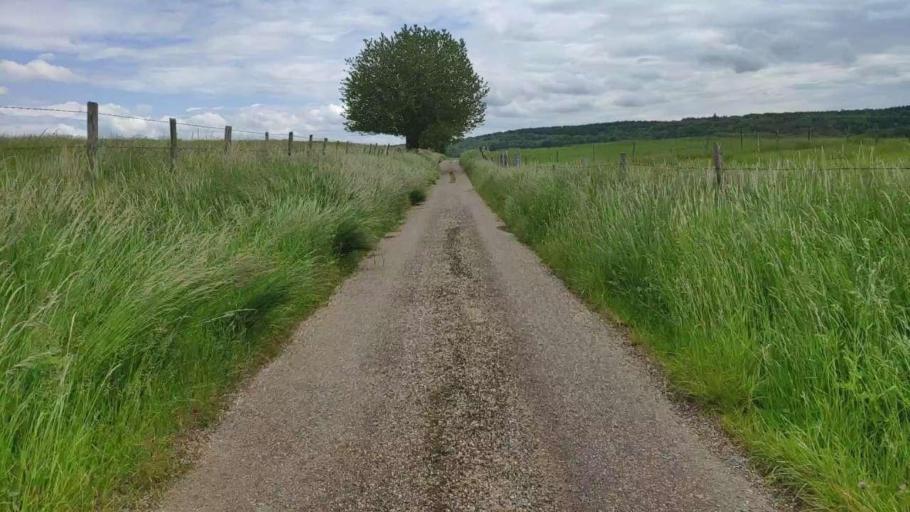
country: FR
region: Franche-Comte
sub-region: Departement du Jura
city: Poligny
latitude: 46.7583
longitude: 5.6382
